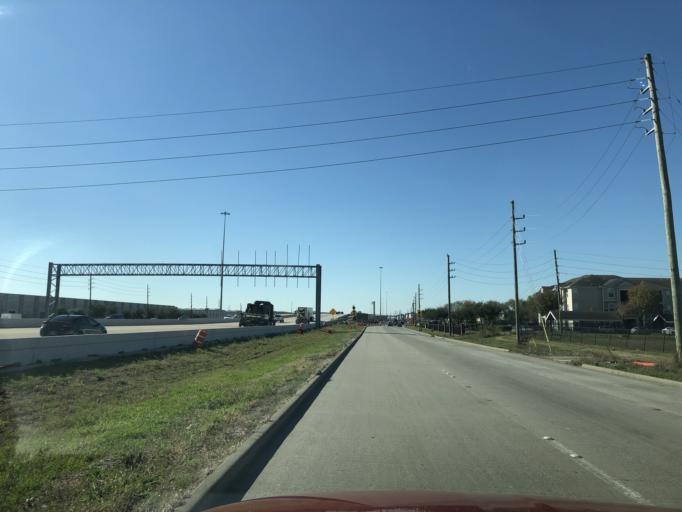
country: US
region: Texas
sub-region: Brazoria County
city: Brookside Village
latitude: 29.5984
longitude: -95.3627
